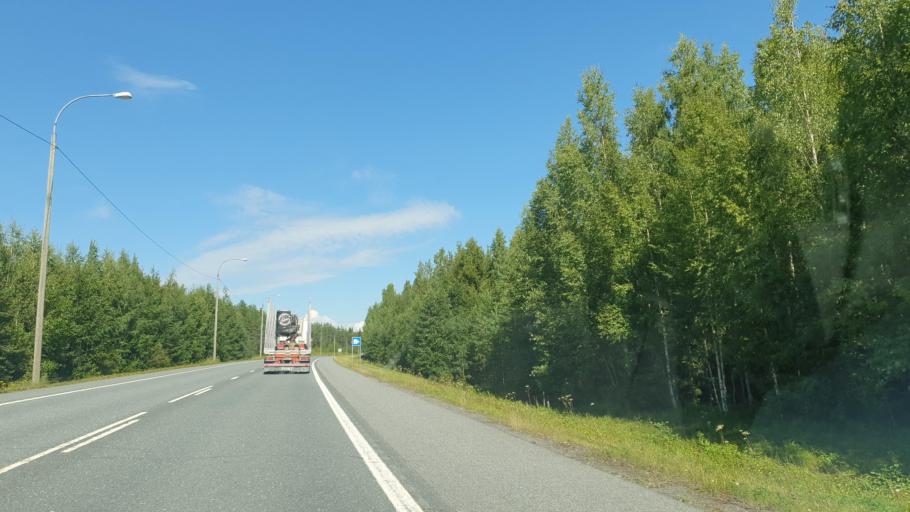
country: FI
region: Northern Savo
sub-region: Ylae-Savo
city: Iisalmi
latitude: 63.5977
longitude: 27.2174
